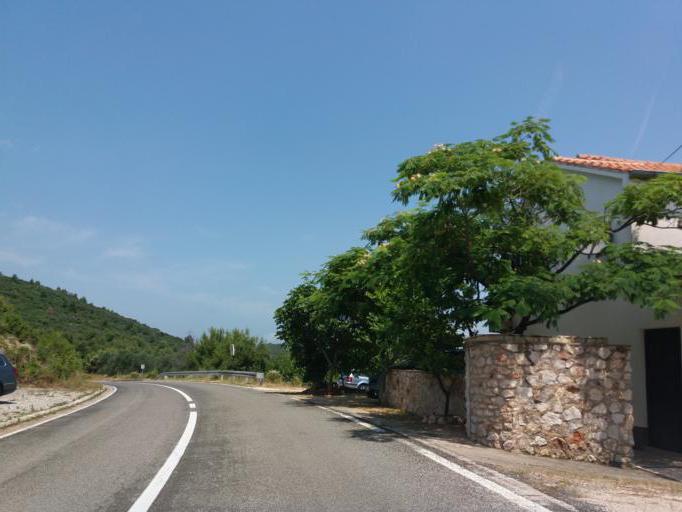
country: HR
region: Zadarska
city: Sali
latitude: 43.9694
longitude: 15.1125
